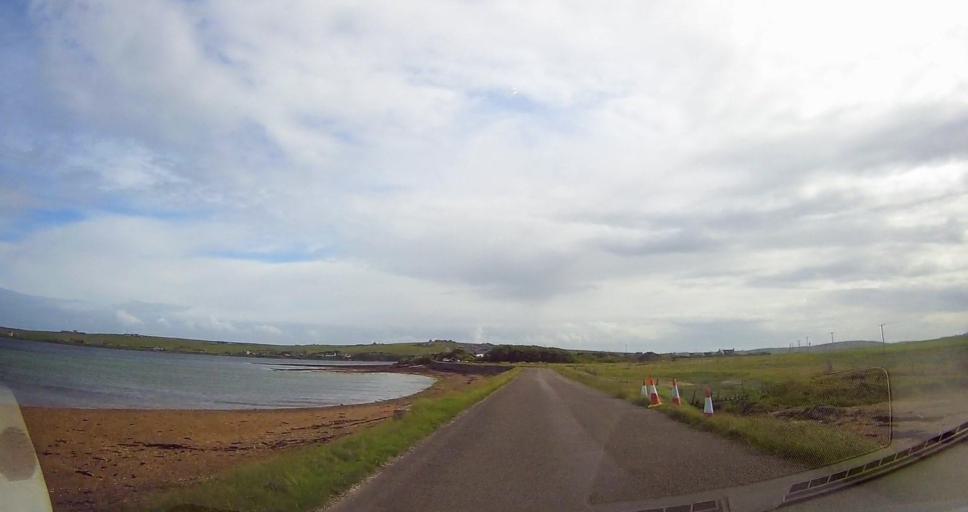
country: GB
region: Scotland
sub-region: Orkney Islands
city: Stromness
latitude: 58.8096
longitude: -3.2033
